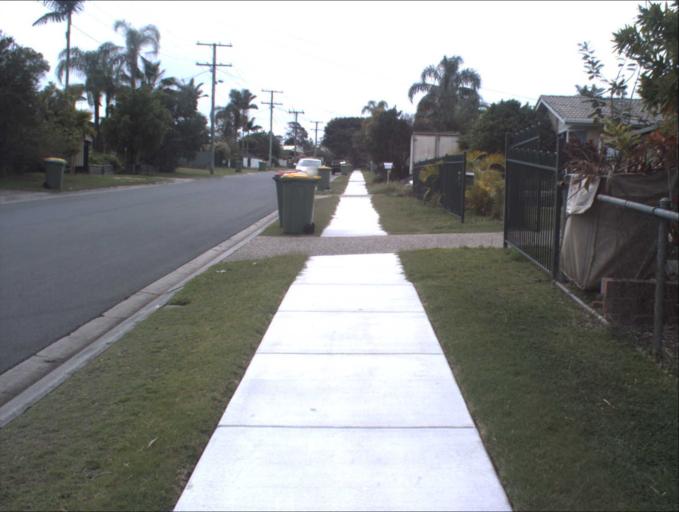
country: AU
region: Queensland
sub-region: Logan
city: Park Ridge South
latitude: -27.6893
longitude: 153.0146
